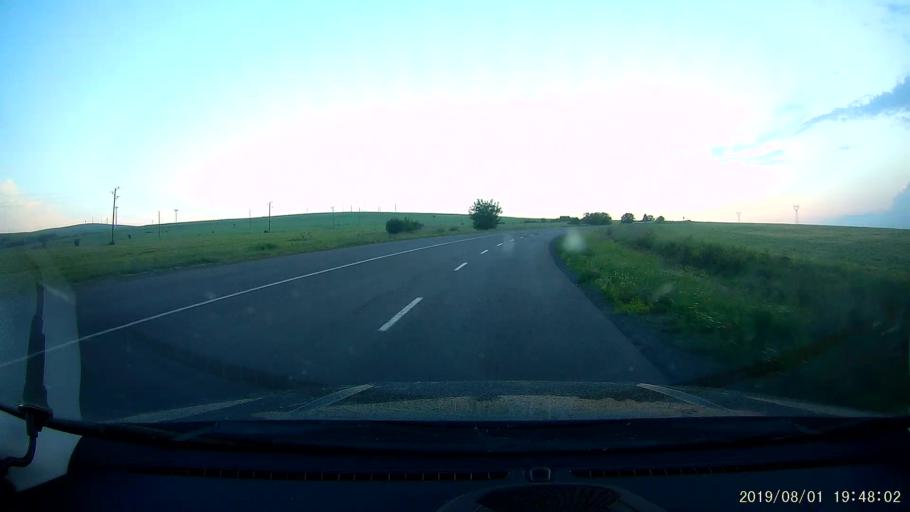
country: BG
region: Burgas
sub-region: Obshtina Karnobat
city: Karnobat
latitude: 42.6424
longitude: 26.9570
